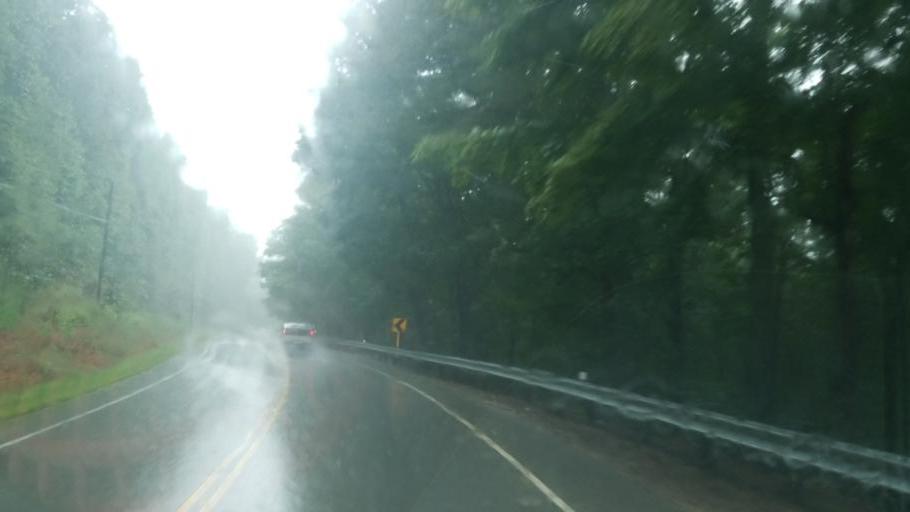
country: US
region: Kentucky
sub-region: Lewis County
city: Vanceburg
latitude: 38.7760
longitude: -83.3247
